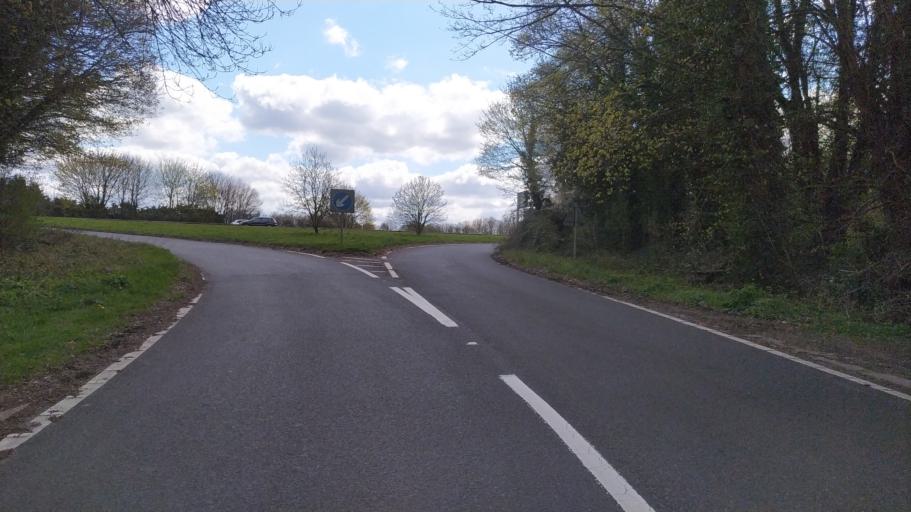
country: GB
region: England
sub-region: Hampshire
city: Abbotts Ann
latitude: 51.2100
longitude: -1.5793
